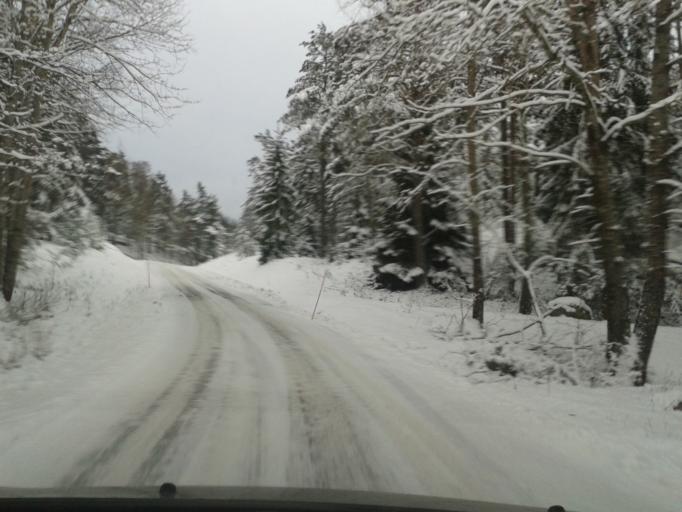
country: SE
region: Stockholm
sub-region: Tyreso Kommun
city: Brevik
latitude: 59.2035
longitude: 18.3204
